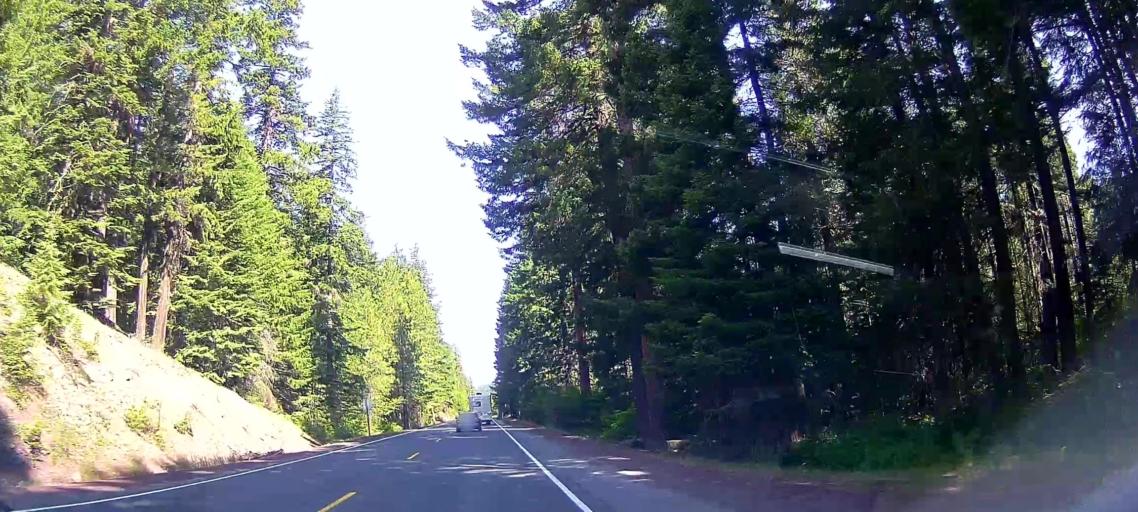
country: US
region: Oregon
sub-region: Jefferson County
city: Warm Springs
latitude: 45.0595
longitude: -121.5167
